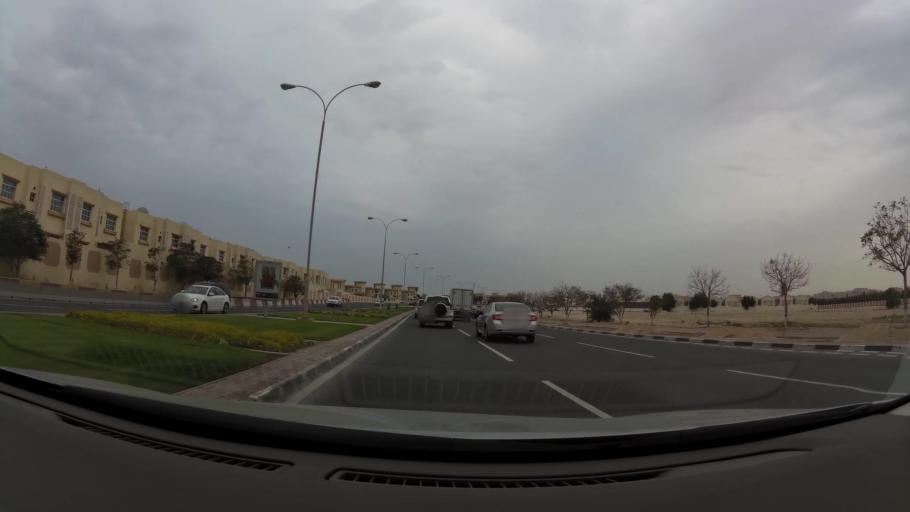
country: QA
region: Baladiyat ad Dawhah
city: Doha
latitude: 25.3267
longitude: 51.4850
